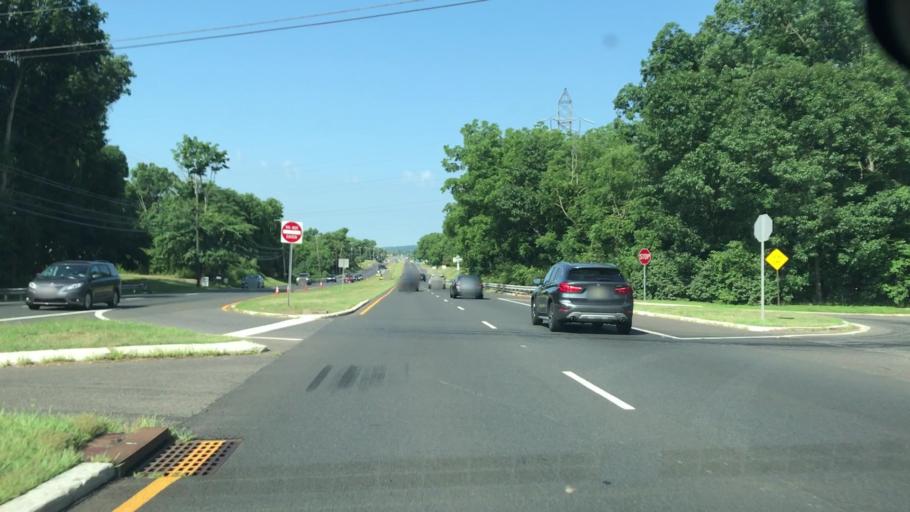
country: US
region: New Jersey
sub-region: Hunterdon County
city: Flemington
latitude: 40.5102
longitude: -74.8350
